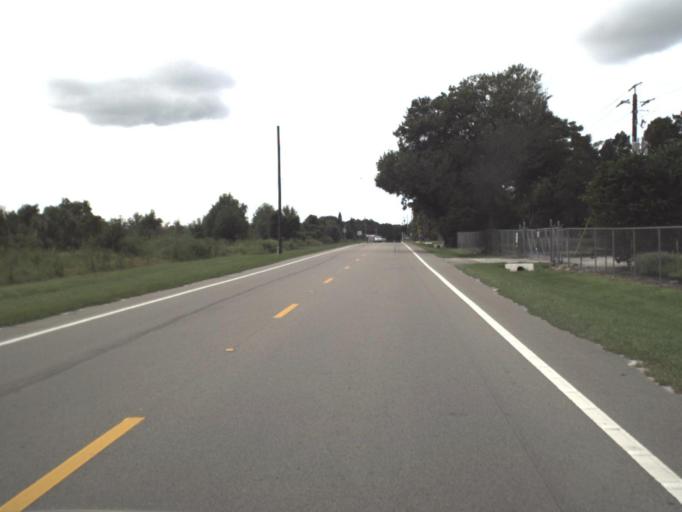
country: US
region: Florida
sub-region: Manatee County
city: Ellenton
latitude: 27.5878
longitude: -82.4192
